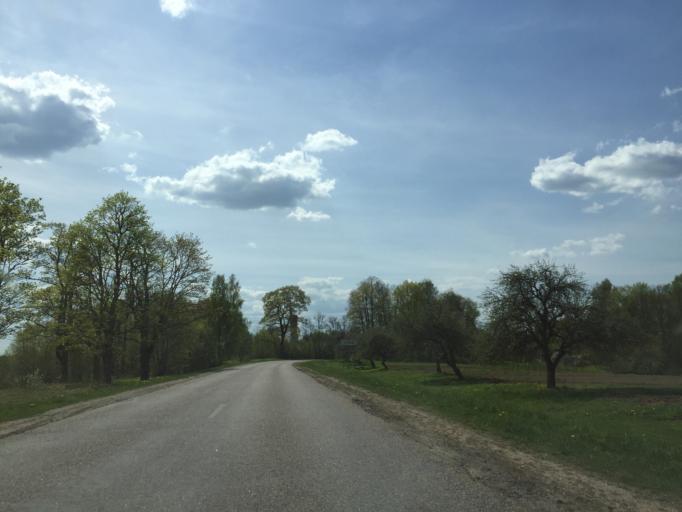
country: LV
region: Limbazu Rajons
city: Limbazi
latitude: 57.3496
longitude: 24.6642
